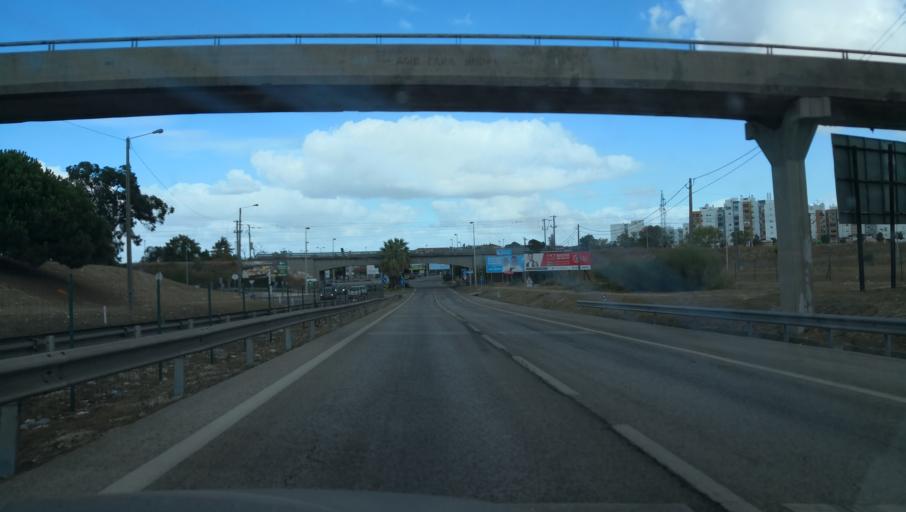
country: PT
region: Setubal
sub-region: Barreiro
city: Barreiro
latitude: 38.6599
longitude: -9.0549
